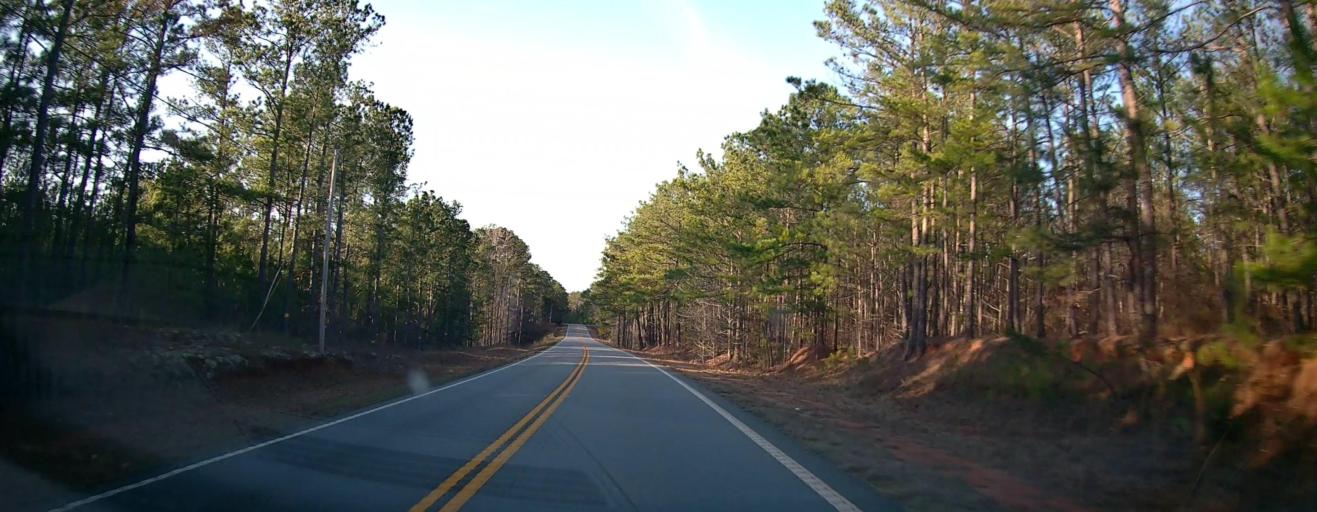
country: US
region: Alabama
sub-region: Chambers County
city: Valley
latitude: 32.7692
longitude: -85.0781
